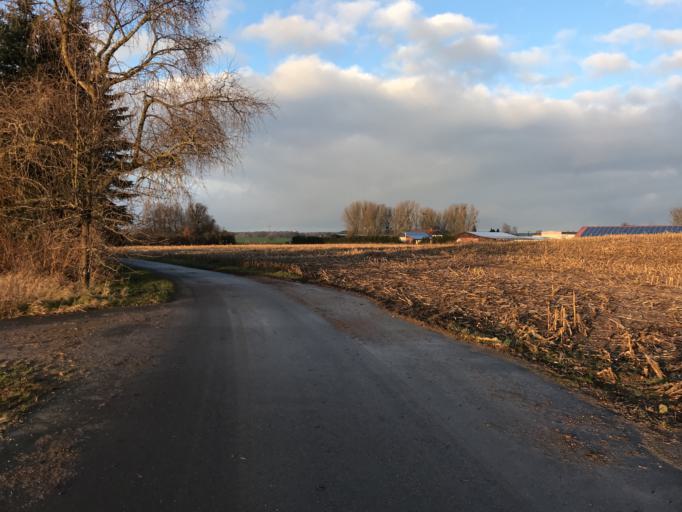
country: DE
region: Mecklenburg-Vorpommern
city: Blankensee
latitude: 53.4093
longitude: 13.2402
